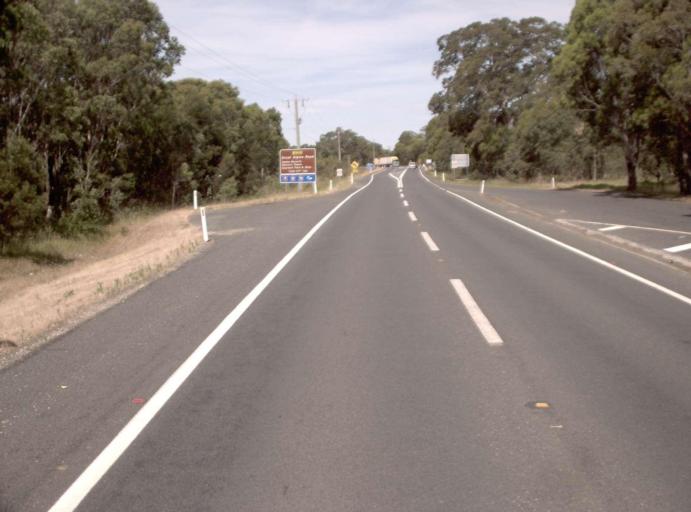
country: AU
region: Victoria
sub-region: East Gippsland
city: Bairnsdale
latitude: -37.8443
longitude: 147.5820
